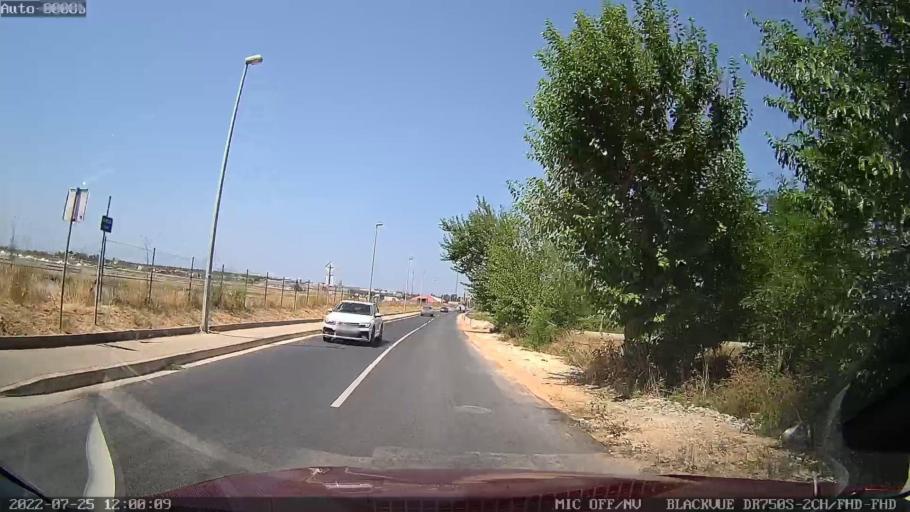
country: HR
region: Zadarska
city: Nin
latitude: 44.2434
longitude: 15.1959
